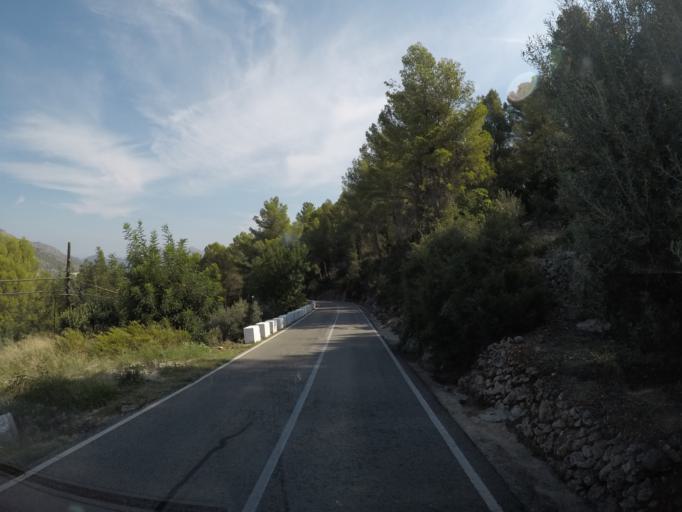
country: ES
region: Valencia
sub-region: Provincia de Alicante
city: Tormos
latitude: 38.7837
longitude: -0.0876
